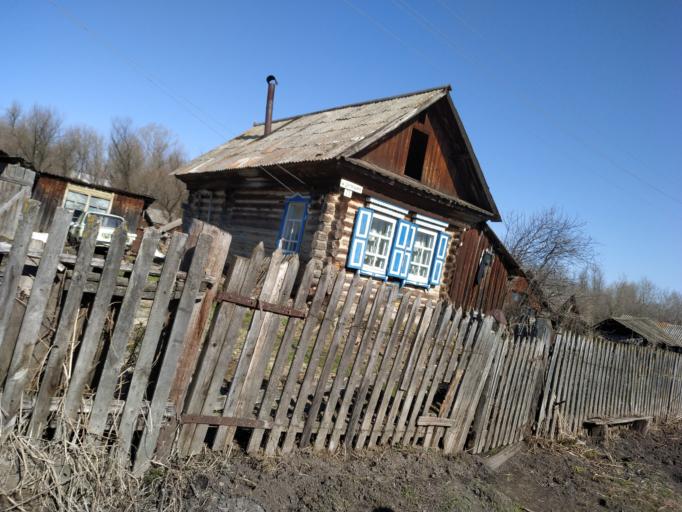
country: RU
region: Altai Krai
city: Krasnogorskoye
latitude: 52.4851
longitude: 86.2331
